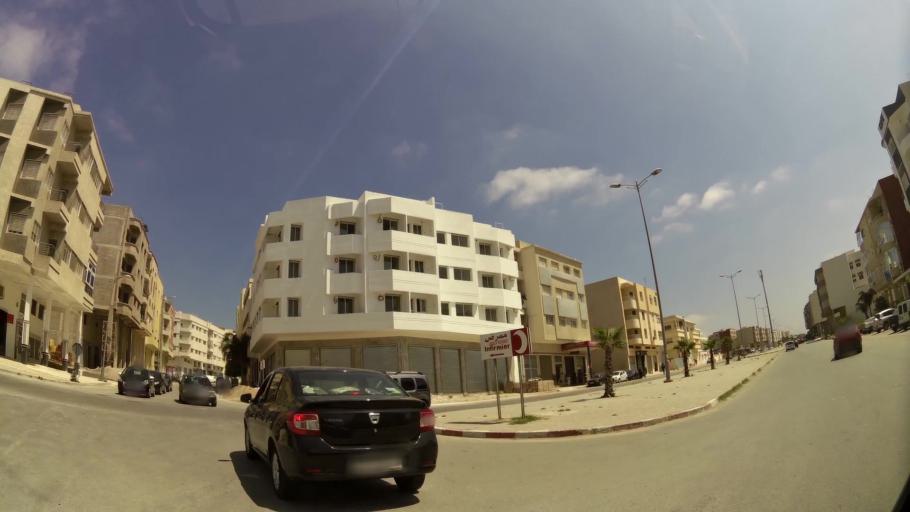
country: MA
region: Fes-Boulemane
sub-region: Fes
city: Fes
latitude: 34.0584
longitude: -5.0293
